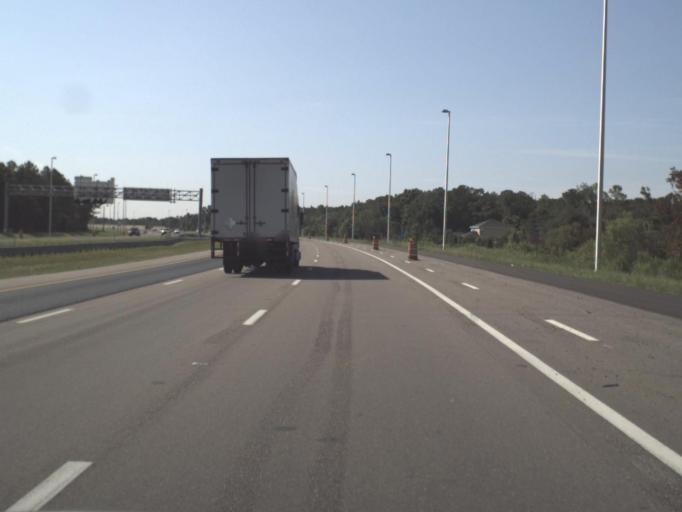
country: US
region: Florida
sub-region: Hillsborough County
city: Pebble Creek
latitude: 28.1039
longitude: -82.3680
